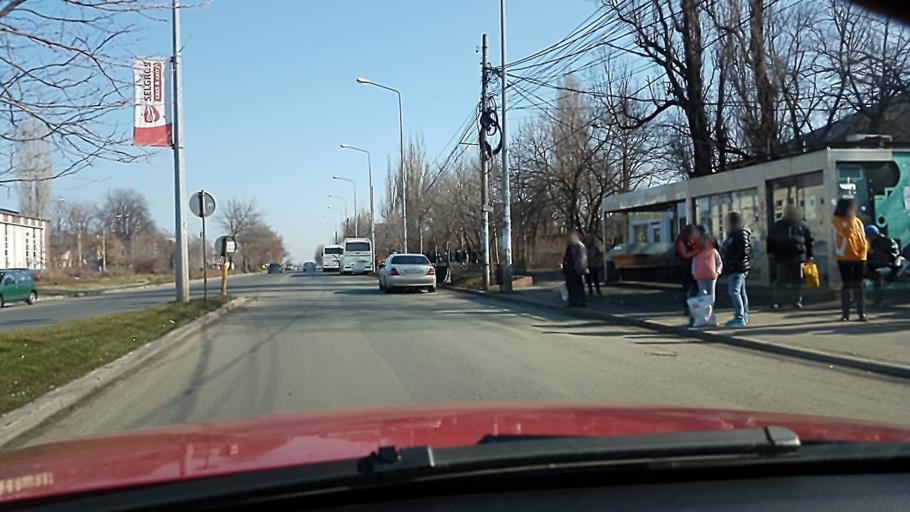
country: RO
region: Ilfov
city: Dobroesti
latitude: 44.4333
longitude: 26.1870
